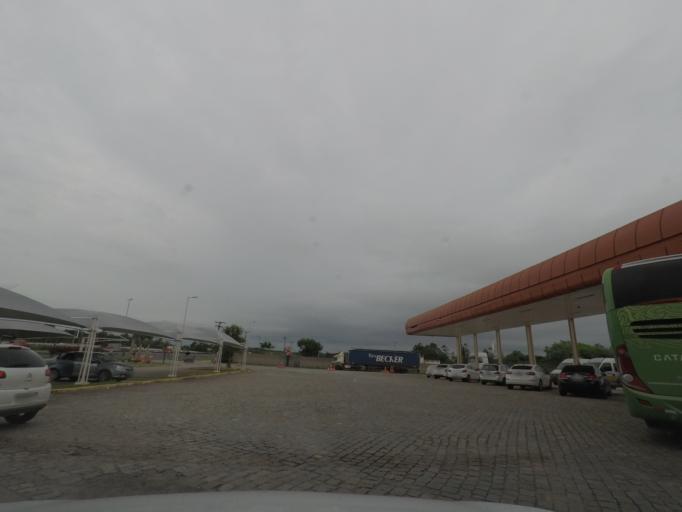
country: BR
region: Sao Paulo
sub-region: Registro
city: Registro
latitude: -24.5304
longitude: -47.8575
